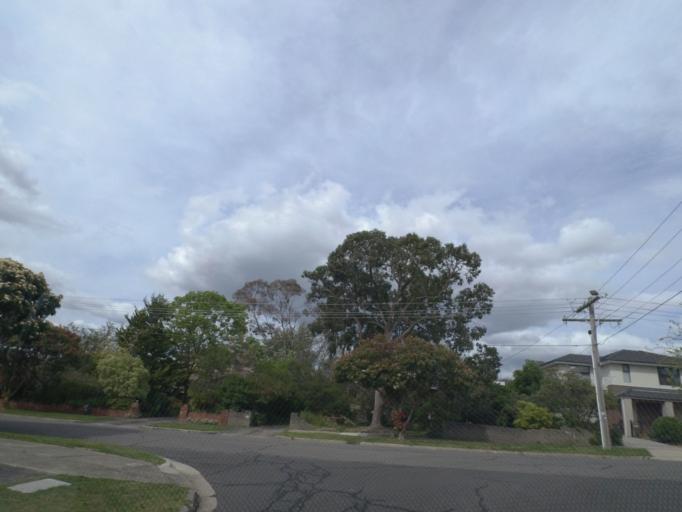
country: AU
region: Victoria
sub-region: Whitehorse
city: Box Hill North
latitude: -37.8088
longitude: 145.1298
